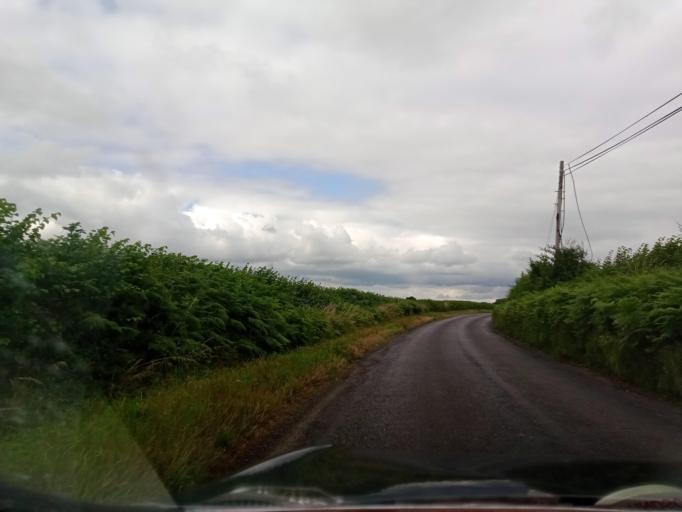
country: IE
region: Leinster
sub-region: Laois
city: Stradbally
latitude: 52.9890
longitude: -7.1810
